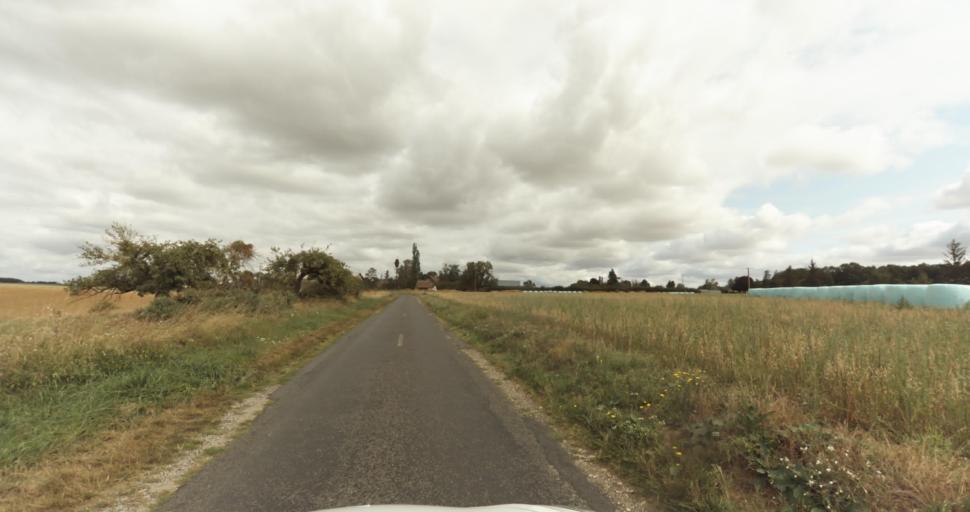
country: FR
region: Haute-Normandie
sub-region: Departement de l'Eure
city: Tillieres-sur-Avre
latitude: 48.7763
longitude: 1.1054
